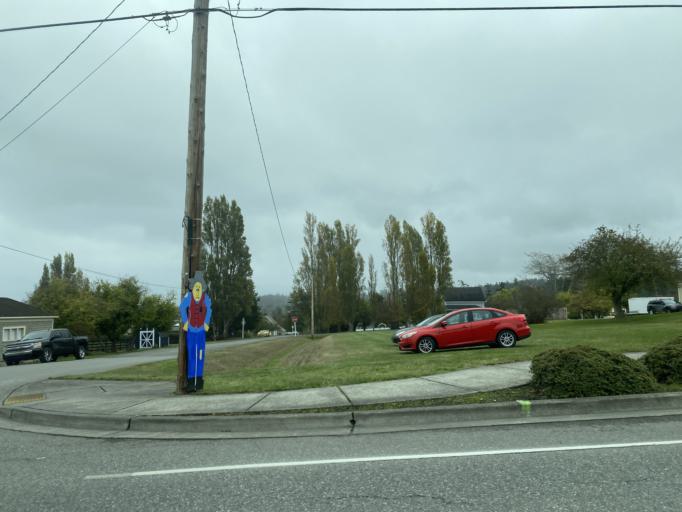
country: US
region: Washington
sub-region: Island County
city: Coupeville
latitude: 48.2193
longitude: -122.6861
